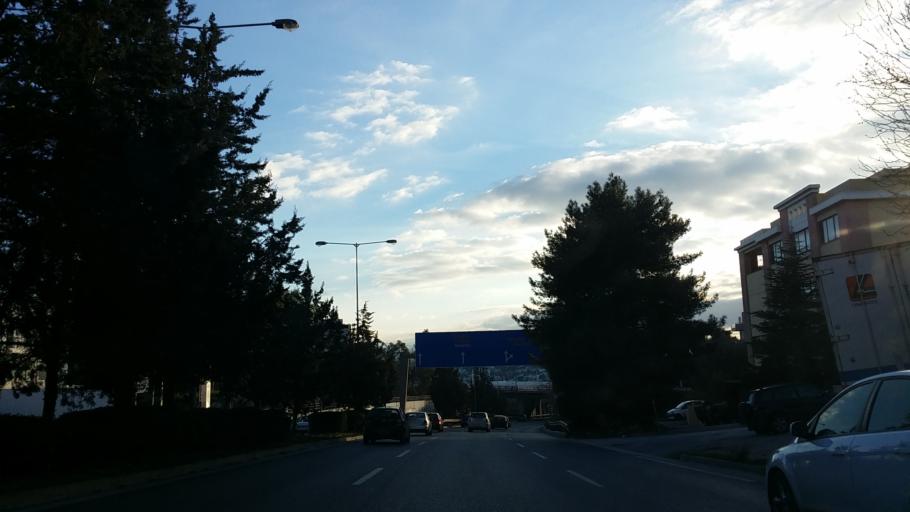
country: GR
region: Attica
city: Pefki
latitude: 38.0465
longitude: 23.7824
